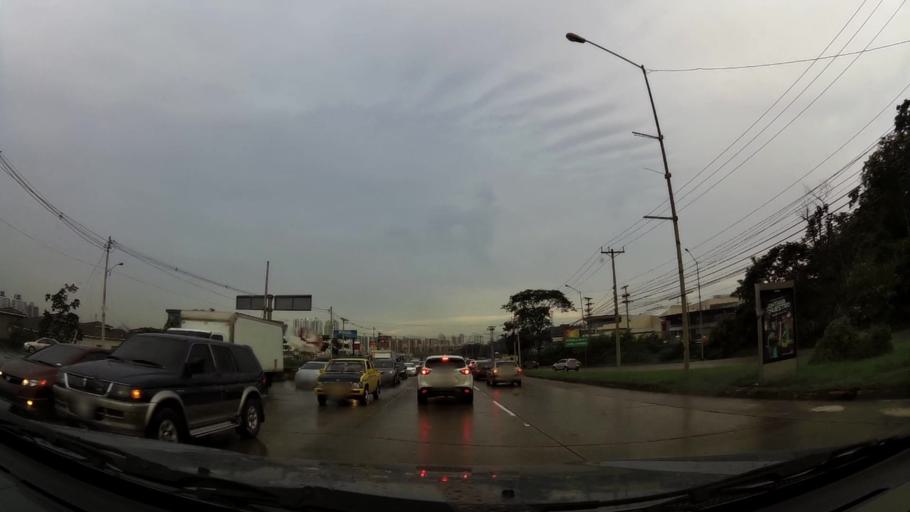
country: PA
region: Panama
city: Panama
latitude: 9.0327
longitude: -79.5357
